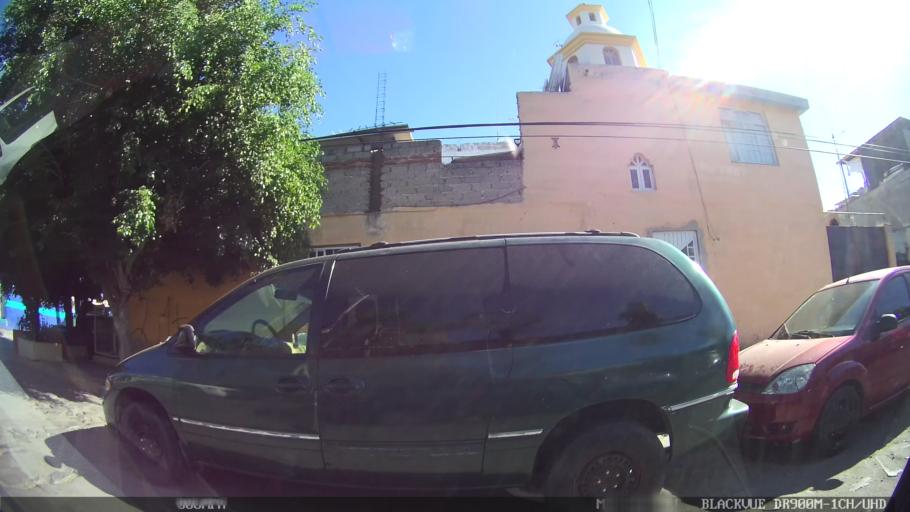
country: MX
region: Jalisco
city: Tlaquepaque
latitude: 20.6874
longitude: -103.2711
